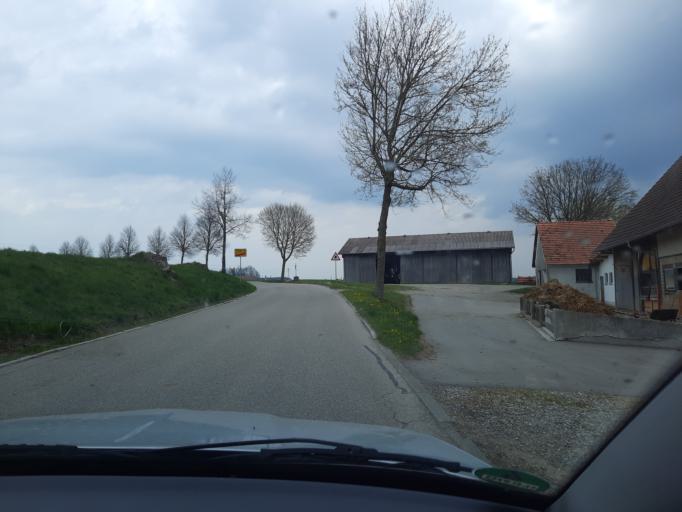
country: DE
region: Baden-Wuerttemberg
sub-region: Tuebingen Region
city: Steinhausen an der Rottum
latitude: 47.9519
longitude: 9.9746
